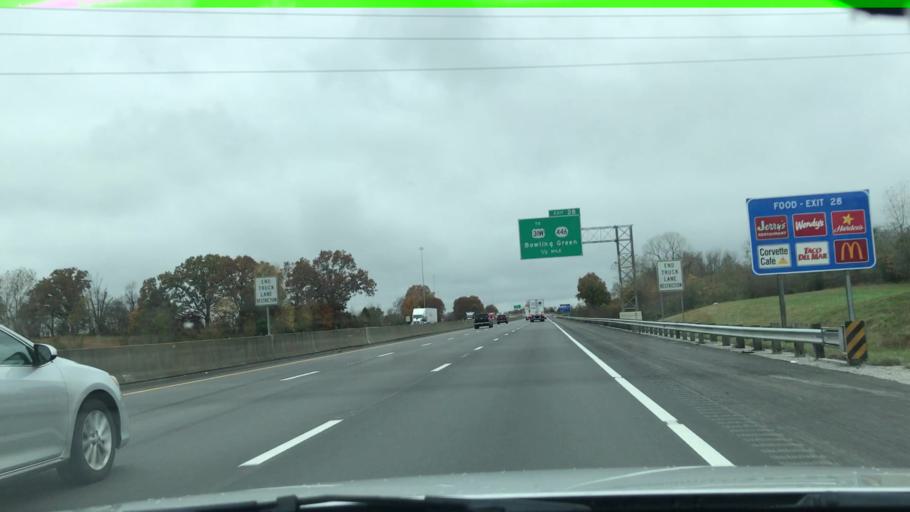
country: US
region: Kentucky
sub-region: Warren County
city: Bowling Green
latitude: 37.0089
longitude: -86.3572
